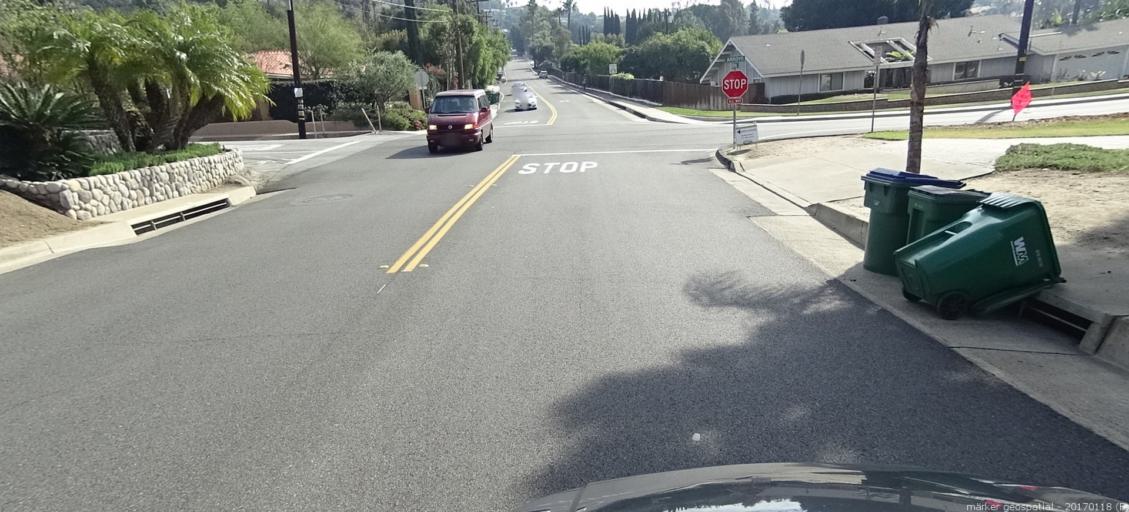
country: US
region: California
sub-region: Orange County
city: North Tustin
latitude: 33.7640
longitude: -117.7912
